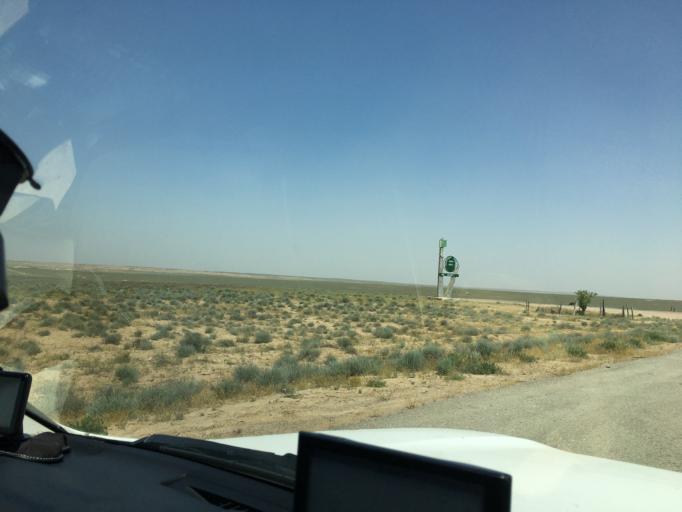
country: TM
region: Balkan
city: Turkmenbasy
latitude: 40.1408
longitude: 53.5218
